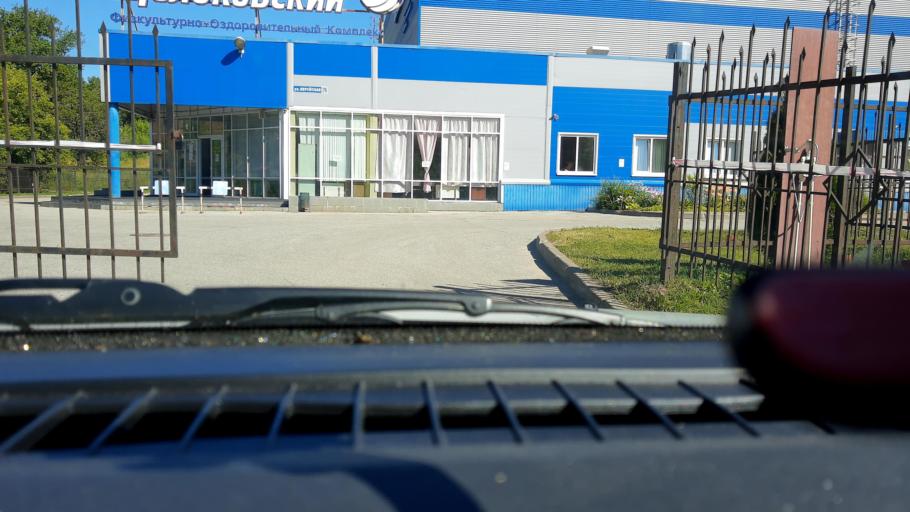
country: RU
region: Nizjnij Novgorod
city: Nizhniy Novgorod
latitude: 56.2735
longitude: 43.9936
